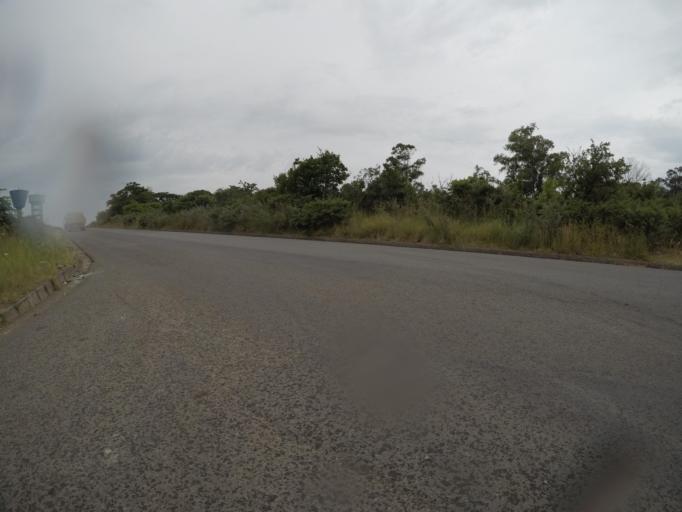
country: ZA
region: Eastern Cape
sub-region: Buffalo City Metropolitan Municipality
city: East London
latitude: -32.9689
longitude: 27.8271
